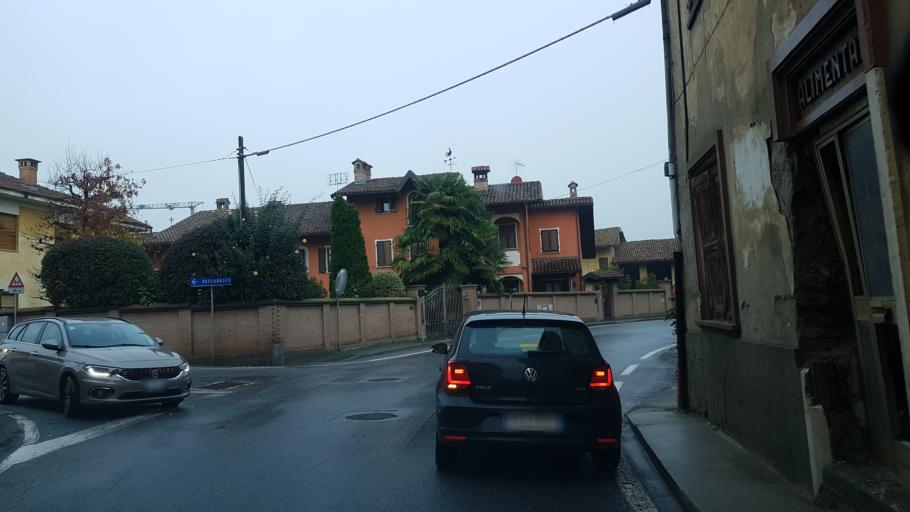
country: IT
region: Piedmont
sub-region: Provincia di Cuneo
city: Vottignasco
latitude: 44.5576
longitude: 7.6216
